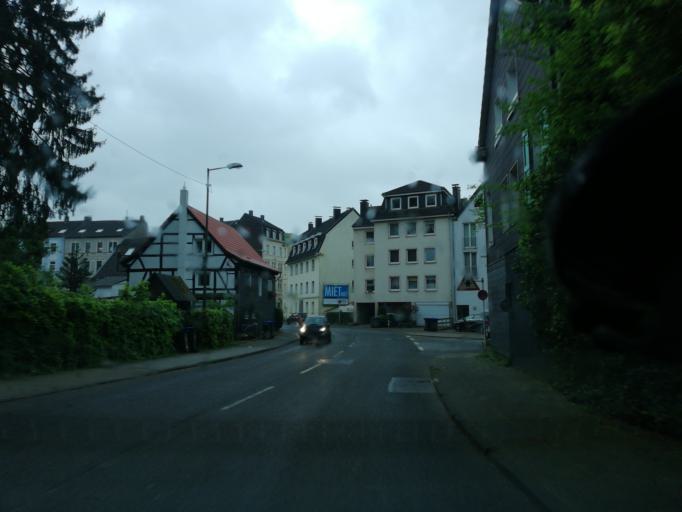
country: DE
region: North Rhine-Westphalia
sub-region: Regierungsbezirk Dusseldorf
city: Solingen
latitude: 51.2389
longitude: 7.0952
